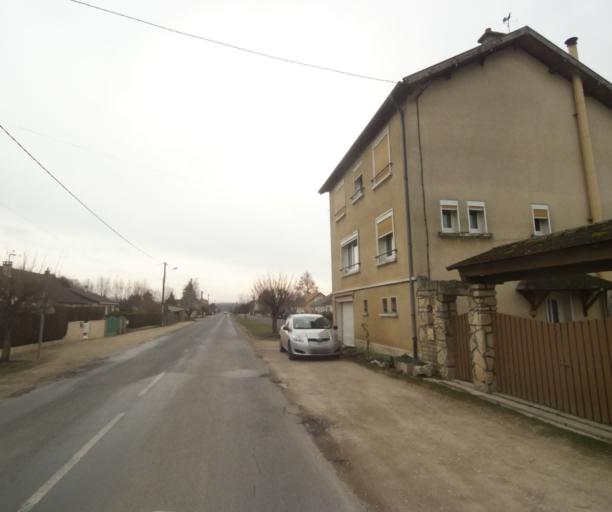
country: FR
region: Champagne-Ardenne
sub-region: Departement de la Haute-Marne
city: Villiers-en-Lieu
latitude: 48.6829
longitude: 4.8832
